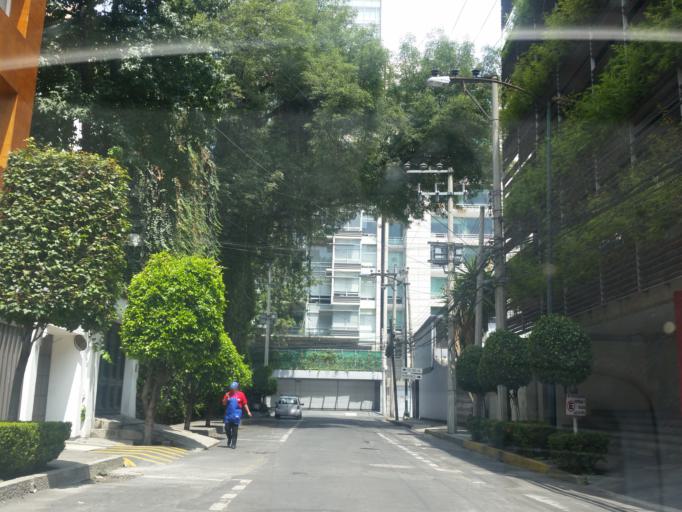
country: MX
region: Mexico City
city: Miguel Hidalgo
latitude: 19.4327
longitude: -99.2108
